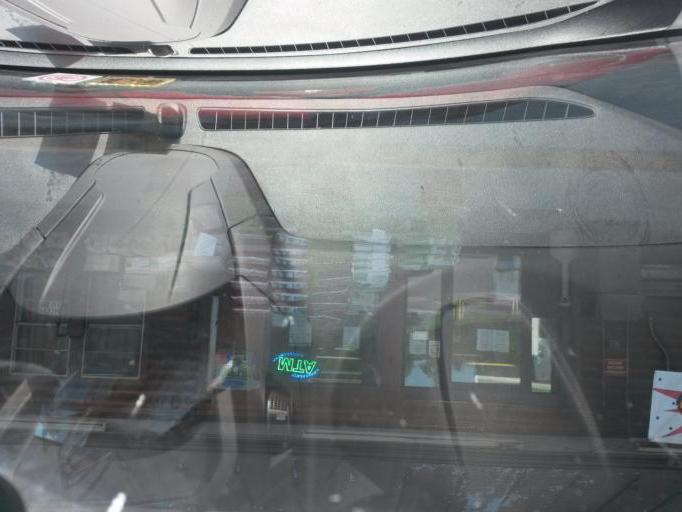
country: US
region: West Virginia
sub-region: Hardy County
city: Moorefield
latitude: 39.0409
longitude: -78.7470
